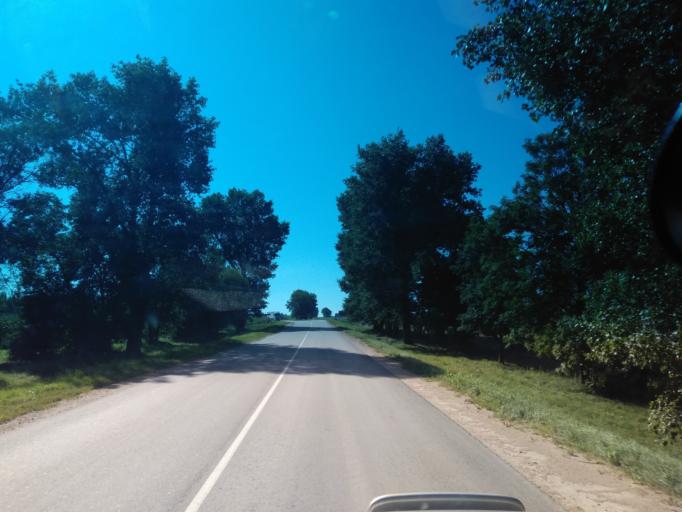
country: BY
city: Fanipol
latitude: 53.6966
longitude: 27.3563
